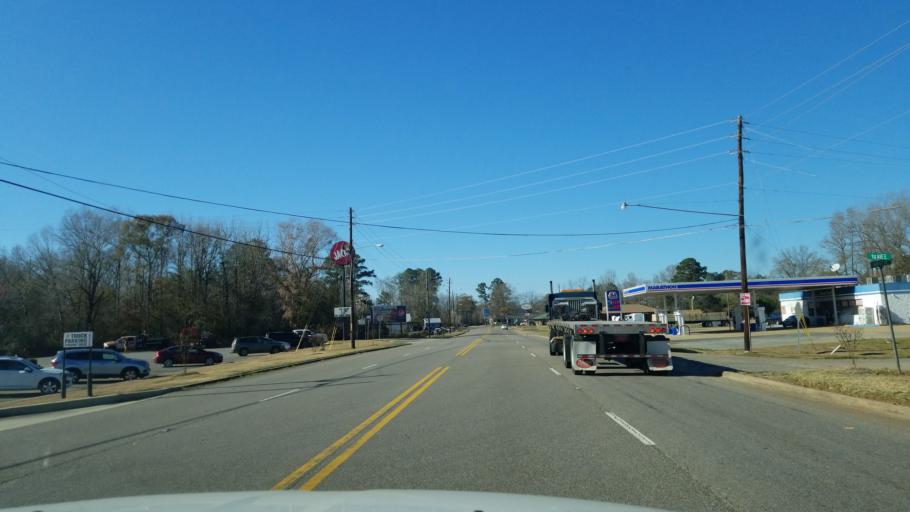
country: US
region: Alabama
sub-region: Pickens County
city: Reform
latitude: 33.3765
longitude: -88.0091
